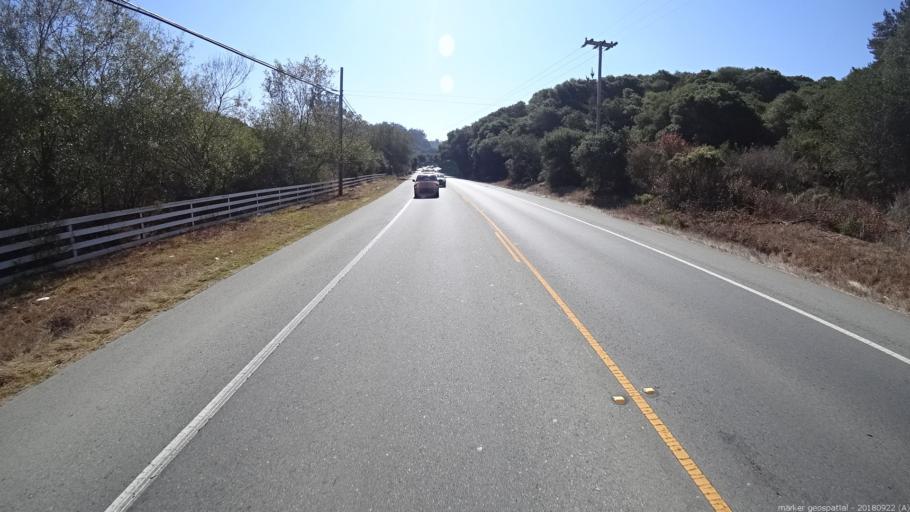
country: US
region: California
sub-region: Monterey County
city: Las Lomas
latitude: 36.8405
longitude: -121.6865
